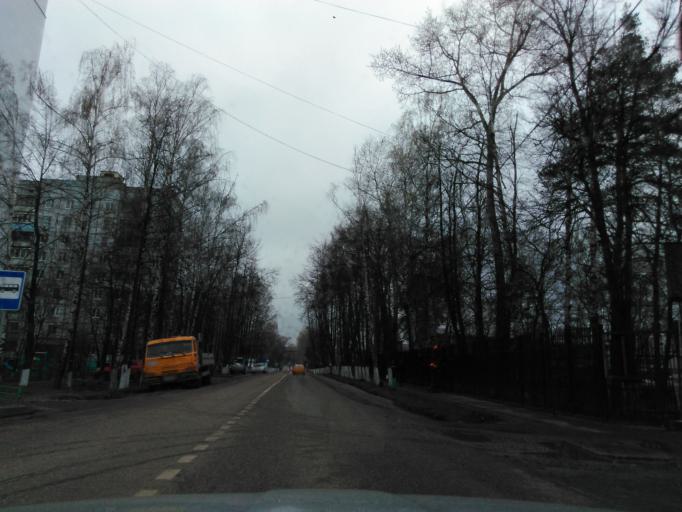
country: RU
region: Moskovskaya
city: Nakhabino
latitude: 55.8406
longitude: 37.1755
